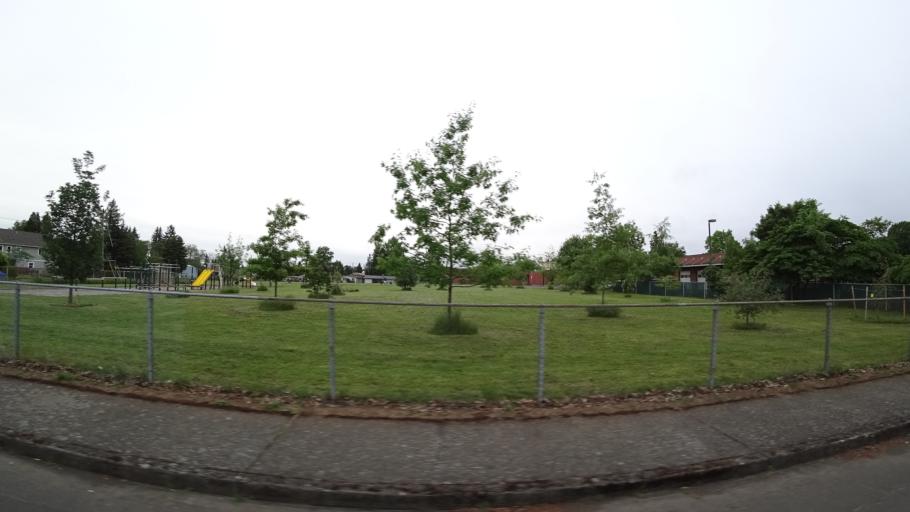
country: US
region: Oregon
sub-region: Multnomah County
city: Portland
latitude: 45.5592
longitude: -122.6234
